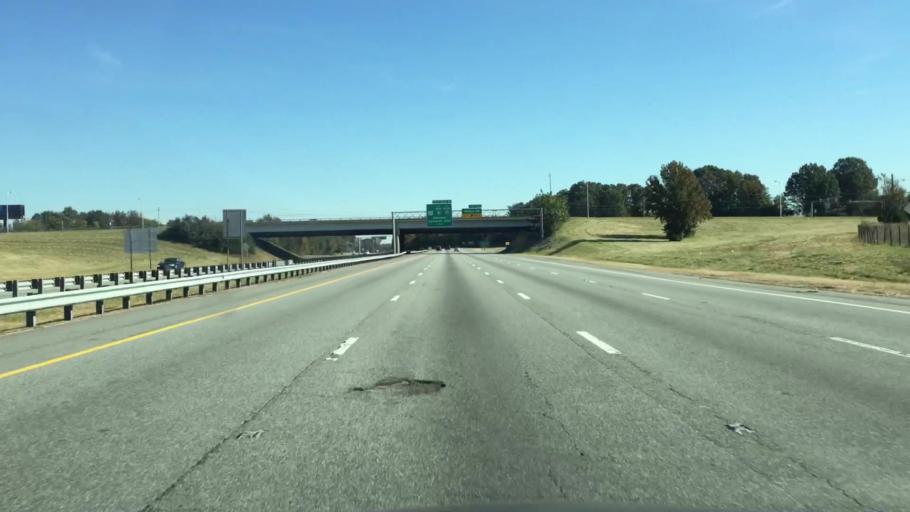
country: US
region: North Carolina
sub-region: Guilford County
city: Greensboro
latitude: 36.0100
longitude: -79.8417
